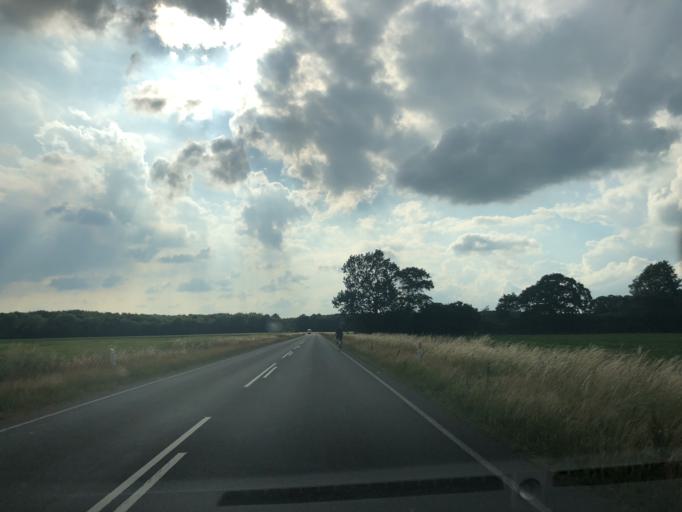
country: DK
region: Zealand
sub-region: Stevns Kommune
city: Harlev
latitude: 55.3161
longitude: 12.1952
